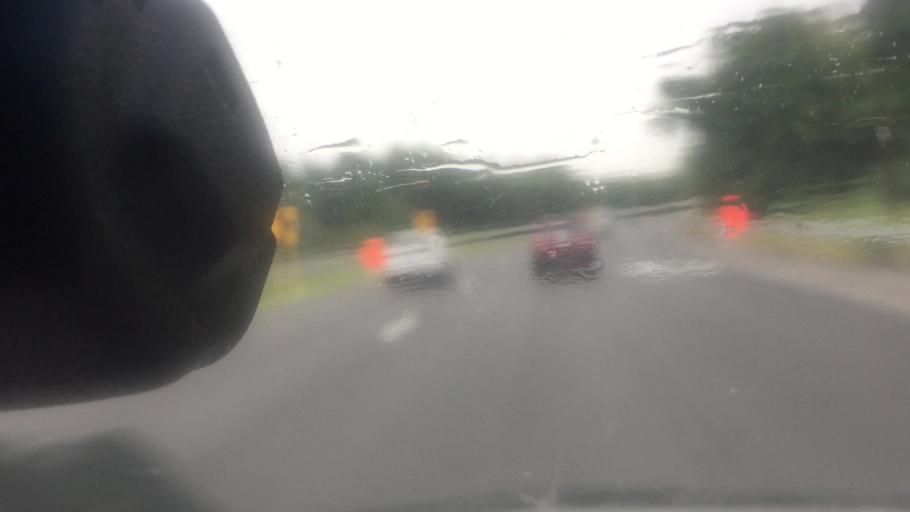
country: US
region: Illinois
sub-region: Sangamon County
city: Southern View
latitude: 39.7565
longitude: -89.6067
